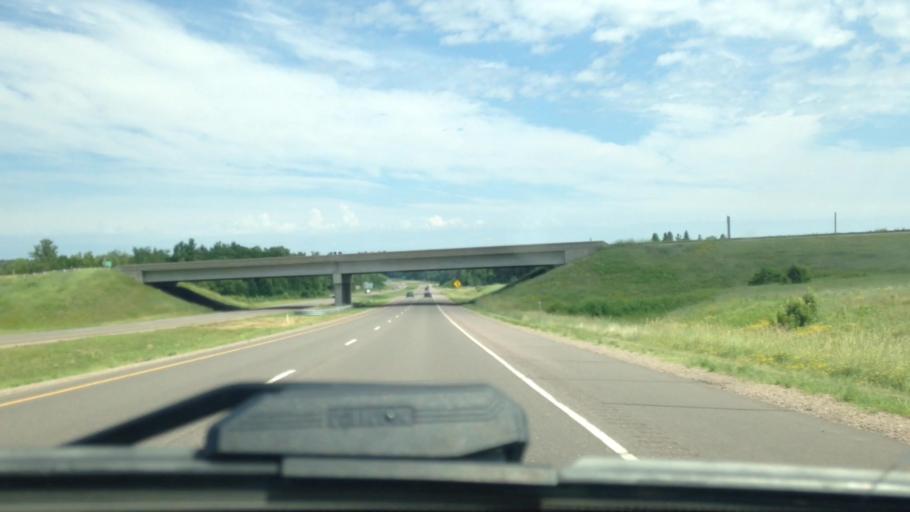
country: US
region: Wisconsin
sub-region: Washburn County
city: Spooner
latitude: 45.8162
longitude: -91.8562
